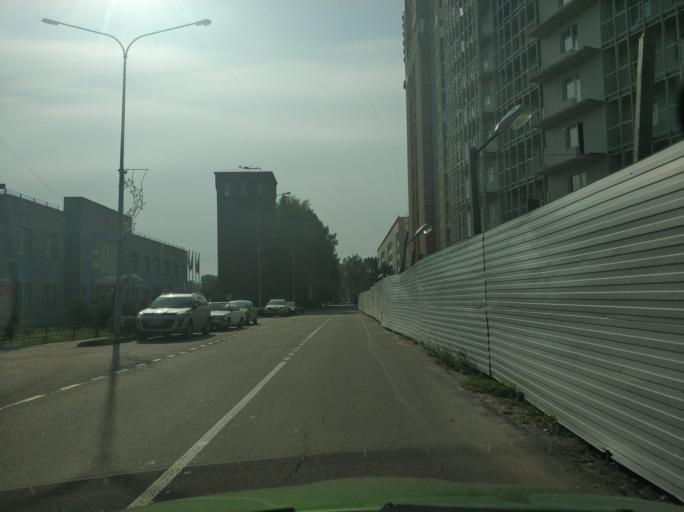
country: RU
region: Leningrad
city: Murino
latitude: 60.0416
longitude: 30.4647
